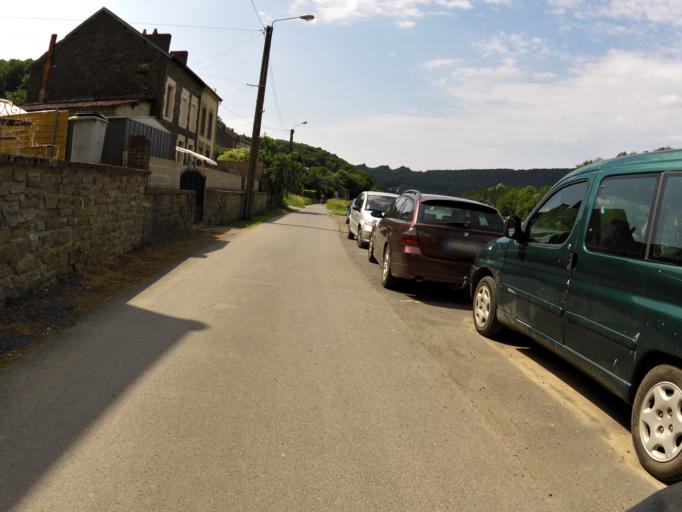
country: FR
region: Champagne-Ardenne
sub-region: Departement des Ardennes
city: Nouzonville
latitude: 49.8531
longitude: 4.7640
